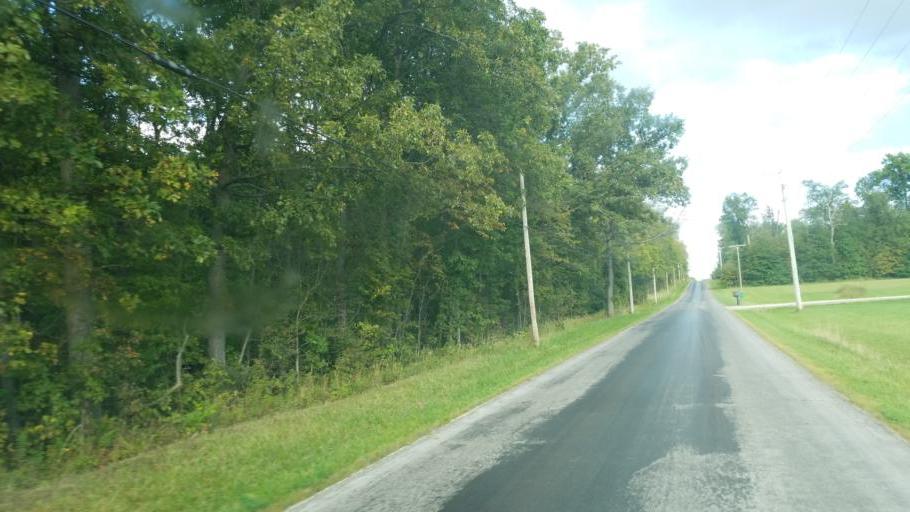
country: US
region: Ohio
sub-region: Huron County
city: Greenwich
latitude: 40.9315
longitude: -82.4894
